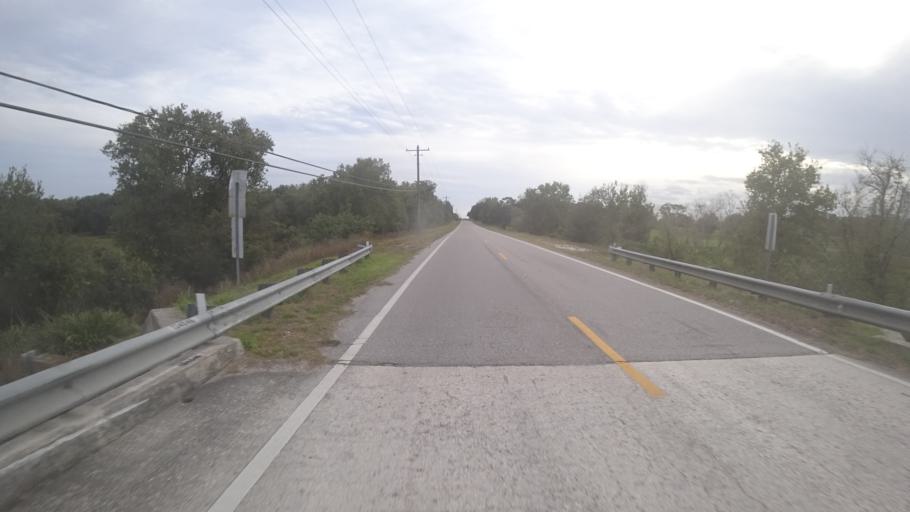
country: US
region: Florida
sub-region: Sarasota County
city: The Meadows
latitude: 27.4669
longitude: -82.2704
